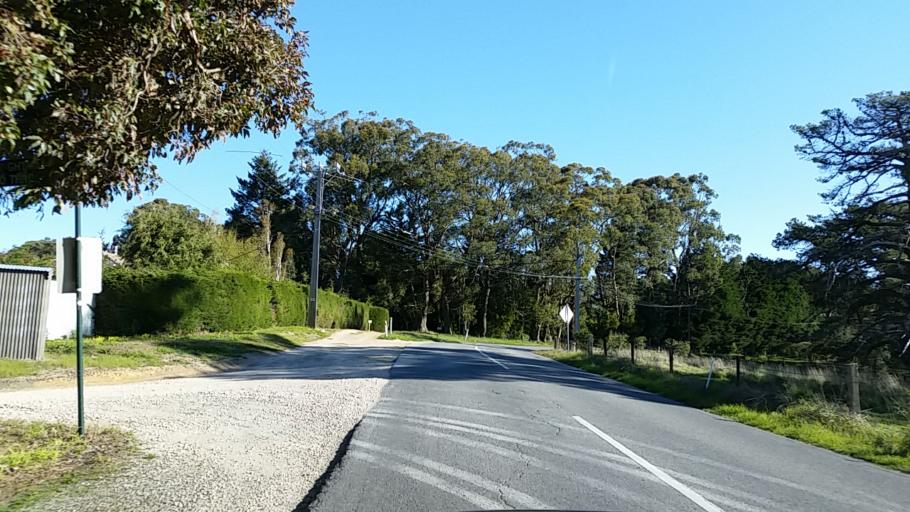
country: AU
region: South Australia
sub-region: Adelaide Hills
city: Adelaide Hills
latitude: -34.9325
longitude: 138.7449
